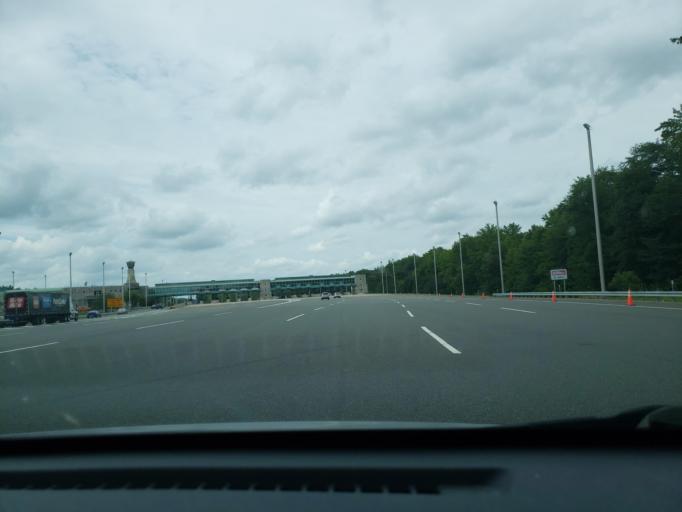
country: US
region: New Jersey
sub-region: Salem County
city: Carneys Point
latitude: 39.6866
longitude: -75.4449
